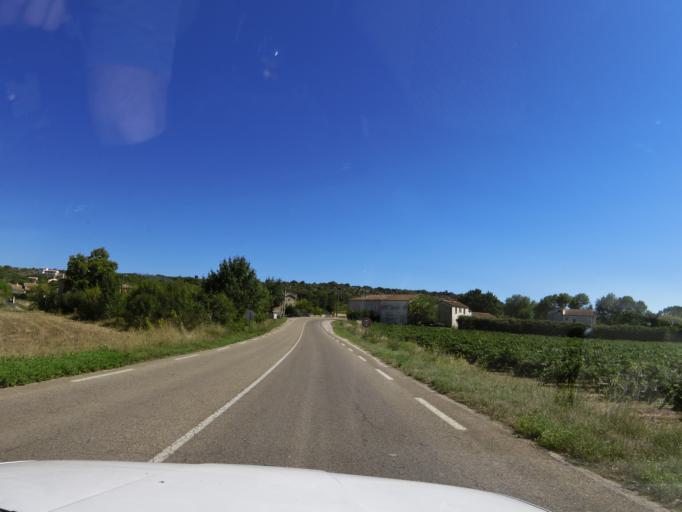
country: FR
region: Languedoc-Roussillon
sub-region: Departement du Gard
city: Saint-Hilaire-de-Brethmas
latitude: 44.0767
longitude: 4.1161
